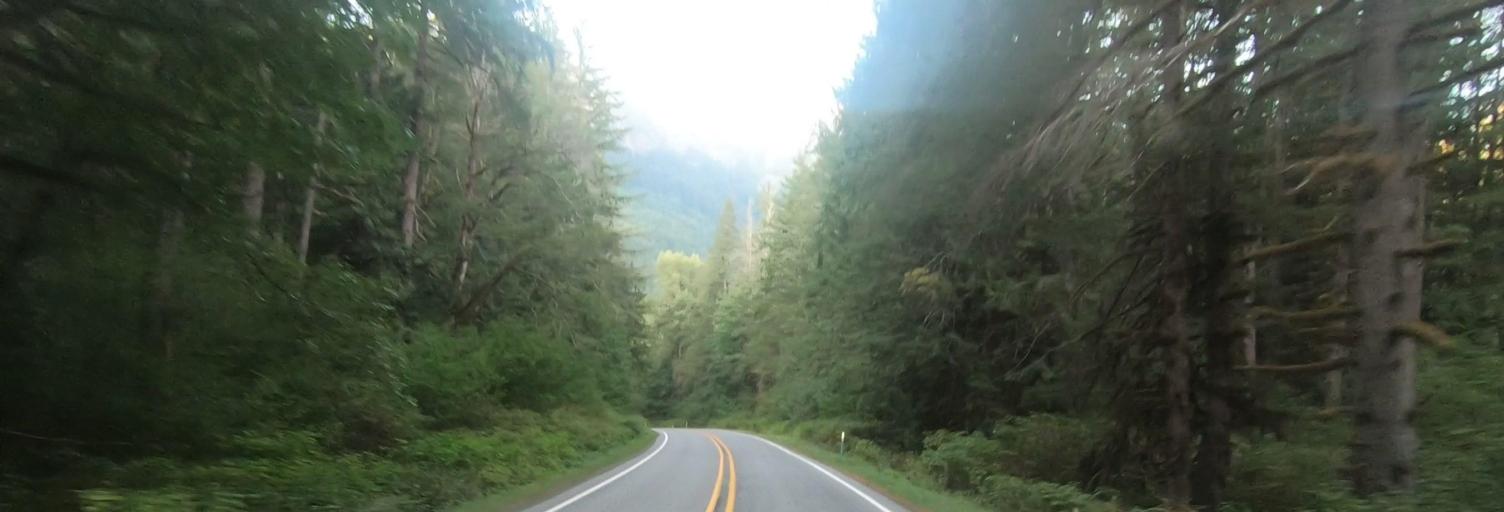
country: US
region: Washington
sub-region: Whatcom County
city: Peaceful Valley
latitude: 48.8997
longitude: -121.9130
